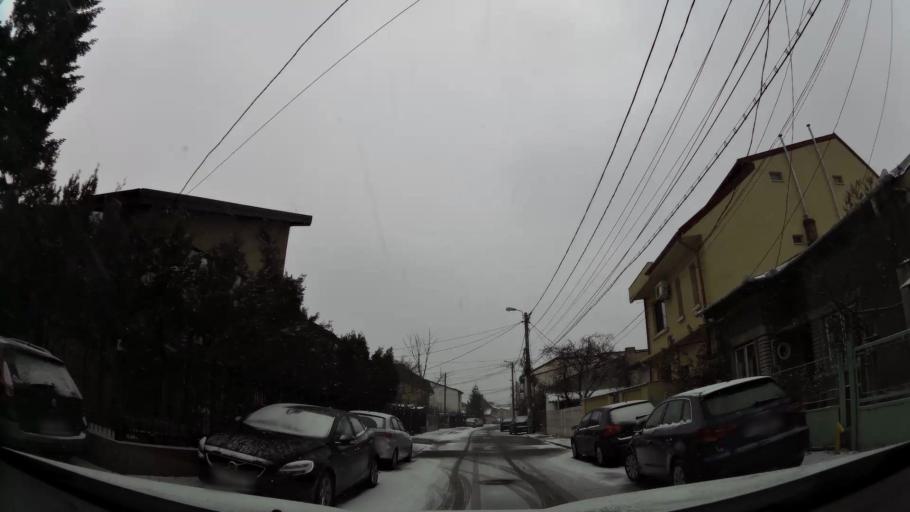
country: RO
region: Prahova
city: Ploiesti
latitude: 44.9429
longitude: 26.0096
